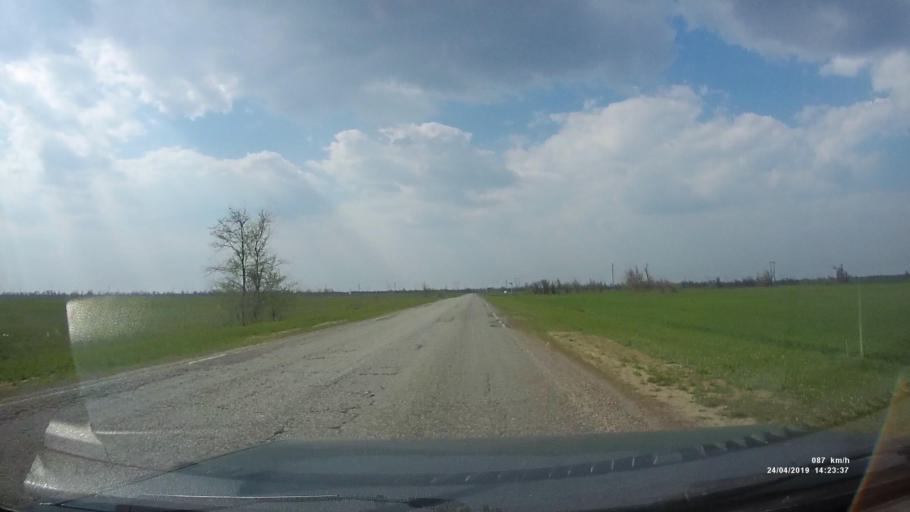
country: RU
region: Kalmykiya
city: Arshan'
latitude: 46.3236
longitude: 44.1118
